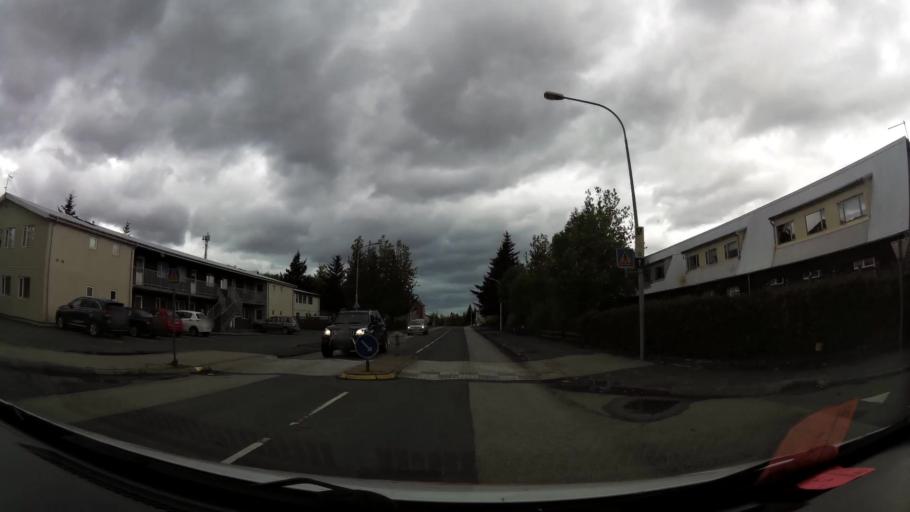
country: IS
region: West
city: Borgarnes
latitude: 64.5412
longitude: -21.9164
